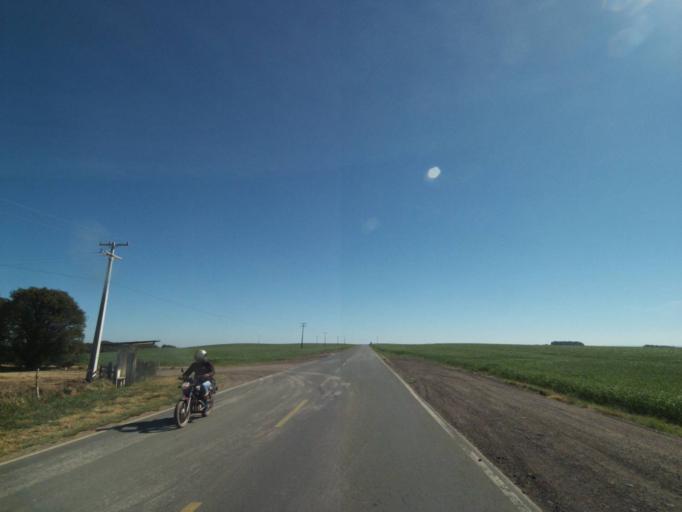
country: BR
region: Parana
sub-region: Tibagi
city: Tibagi
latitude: -24.5709
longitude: -50.2806
